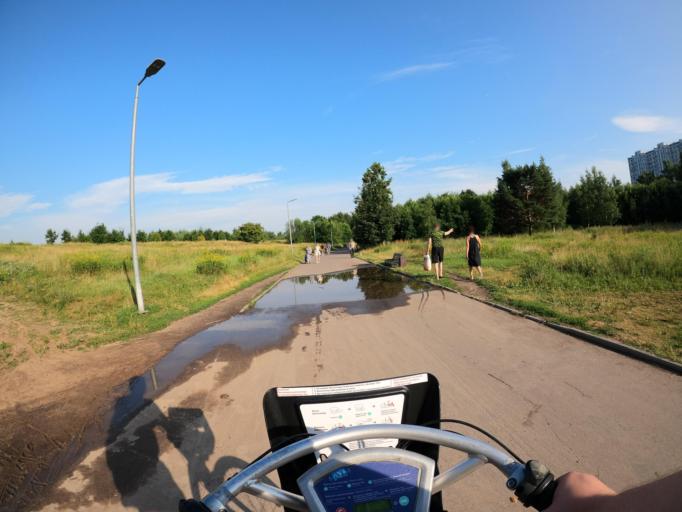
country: RU
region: Moscow
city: Strogino
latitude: 55.8165
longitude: 37.4083
